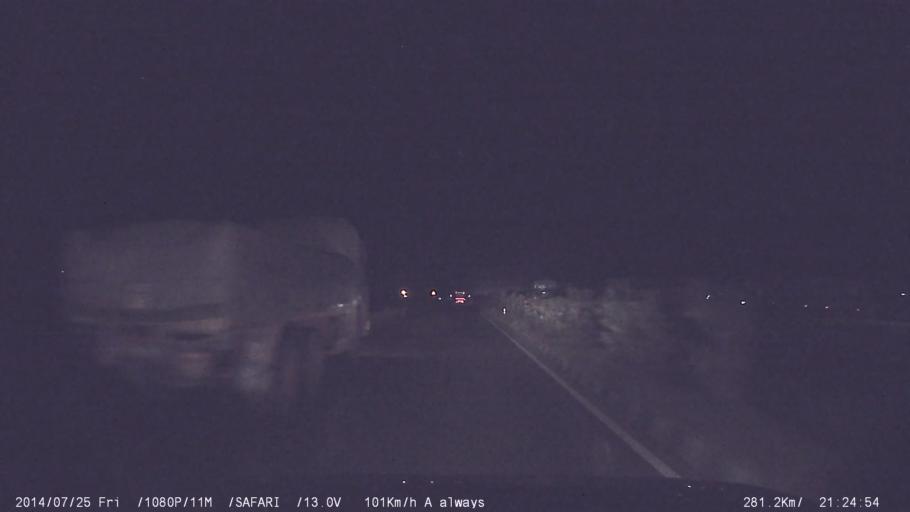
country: IN
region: Tamil Nadu
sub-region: Erode
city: Perundurai
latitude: 11.2554
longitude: 77.5469
